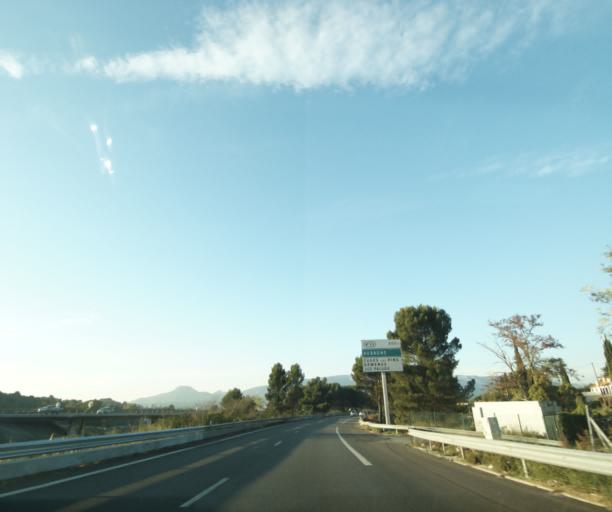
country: FR
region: Provence-Alpes-Cote d'Azur
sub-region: Departement des Bouches-du-Rhone
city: Aubagne
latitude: 43.2792
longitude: 5.5855
